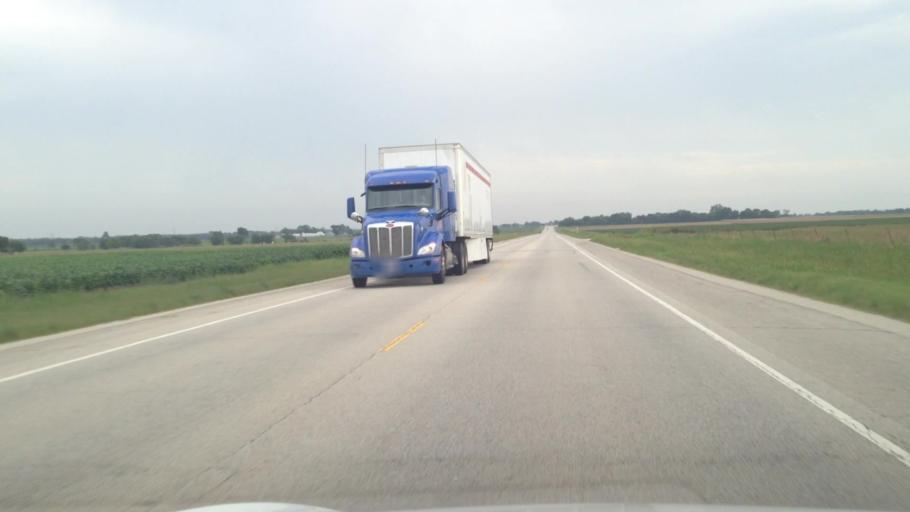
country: US
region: Oklahoma
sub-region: Ottawa County
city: Afton
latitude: 36.6429
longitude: -94.9815
